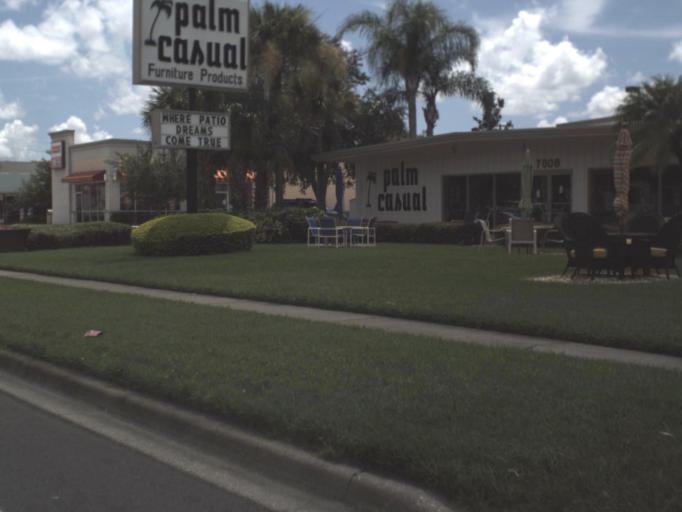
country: US
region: Florida
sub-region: Hillsborough County
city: Egypt Lake-Leto
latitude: 28.0133
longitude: -82.5051
